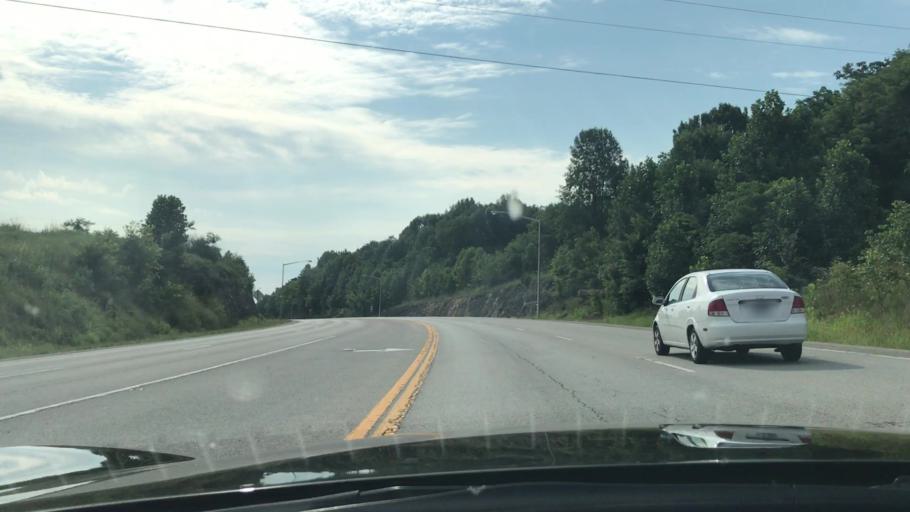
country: US
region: Kentucky
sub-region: Green County
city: Greensburg
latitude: 37.2738
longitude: -85.5078
